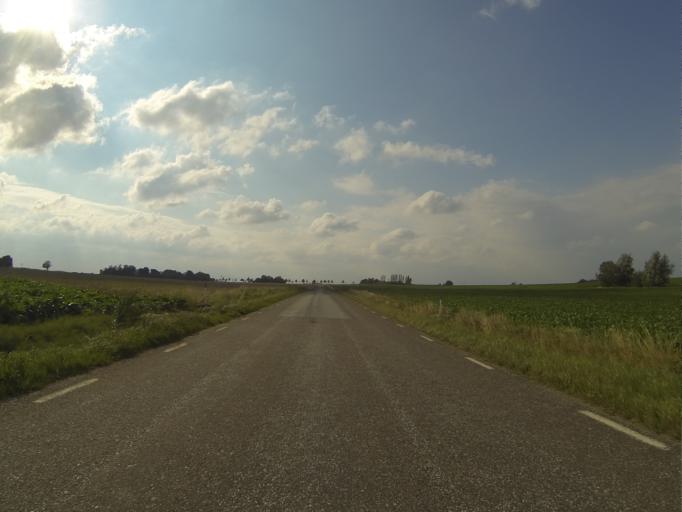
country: SE
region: Skane
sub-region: Lunds Kommun
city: Lund
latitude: 55.7494
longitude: 13.2421
